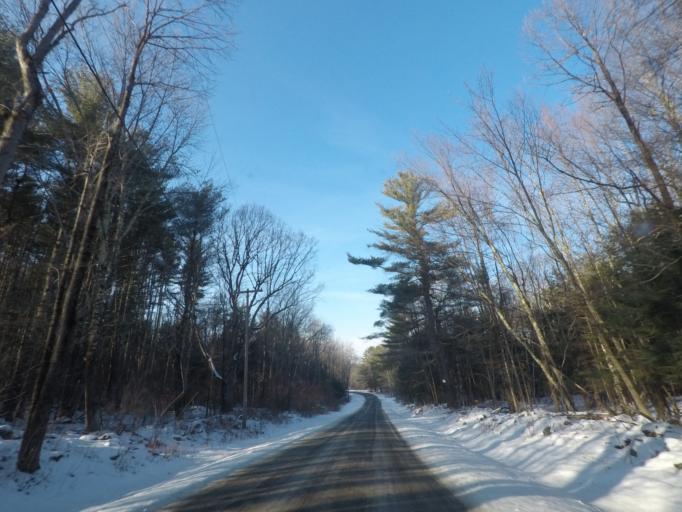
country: US
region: New York
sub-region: Rensselaer County
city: Nassau
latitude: 42.5003
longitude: -73.5042
